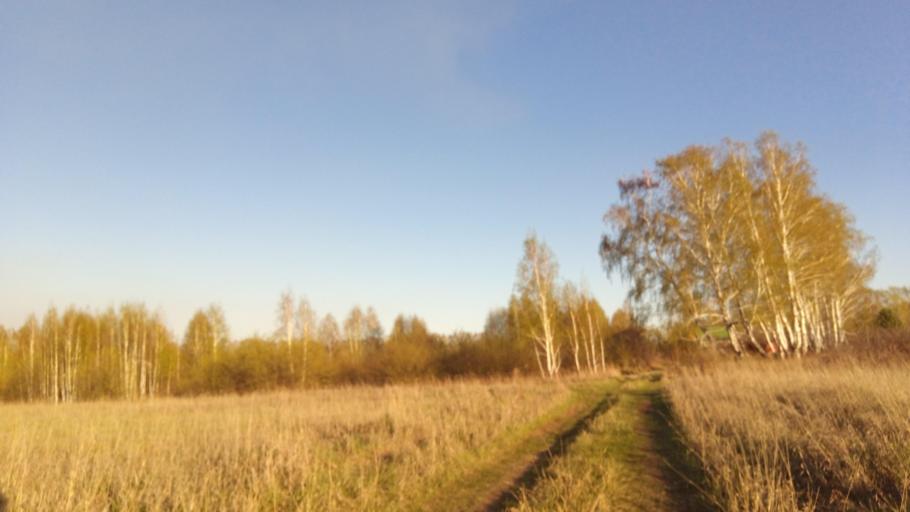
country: RU
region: Chelyabinsk
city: Timiryazevskiy
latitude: 54.9915
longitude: 60.8538
